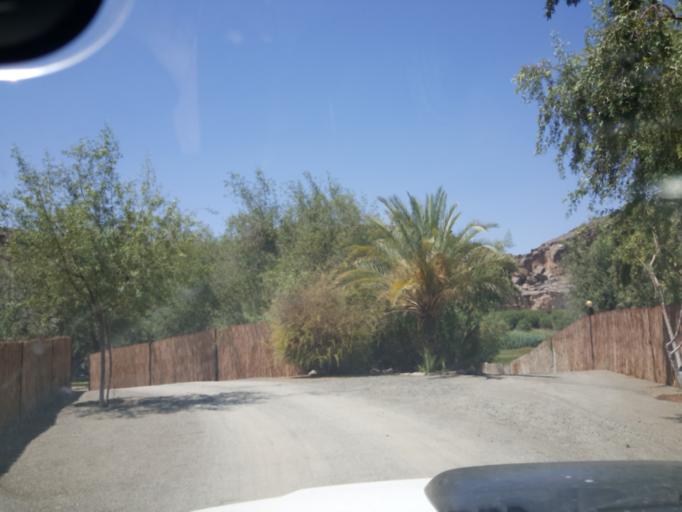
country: ZA
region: Northern Cape
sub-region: Namakwa District Municipality
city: Port Nolloth
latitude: -28.6994
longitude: 17.5322
